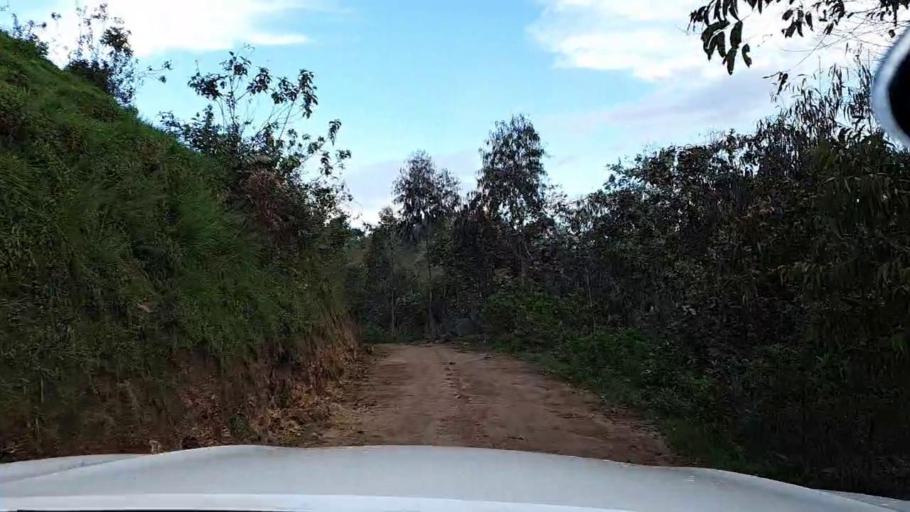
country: BI
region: Kayanza
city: Kayanza
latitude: -2.7794
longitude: 29.4490
